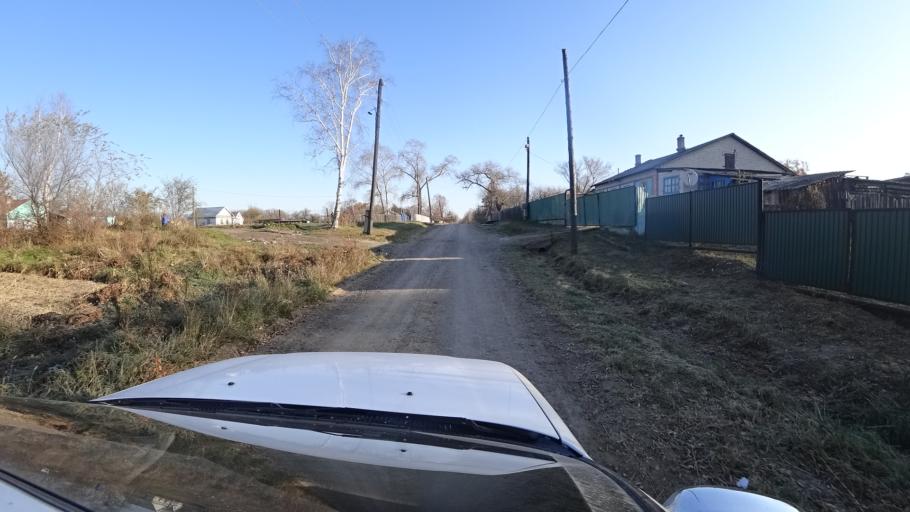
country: RU
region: Primorskiy
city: Lazo
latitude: 45.8721
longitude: 133.6448
